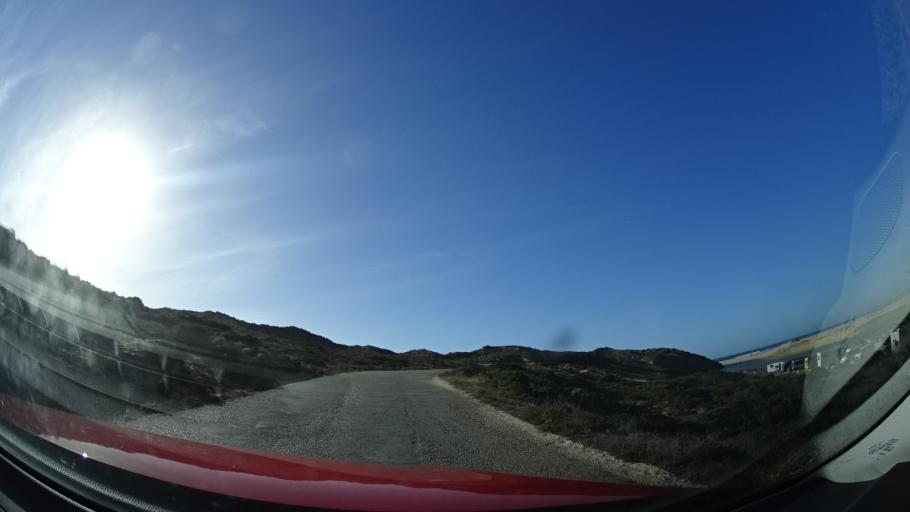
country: PT
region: Faro
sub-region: Vila do Bispo
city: Vila do Bispo
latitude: 37.1920
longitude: -8.9028
